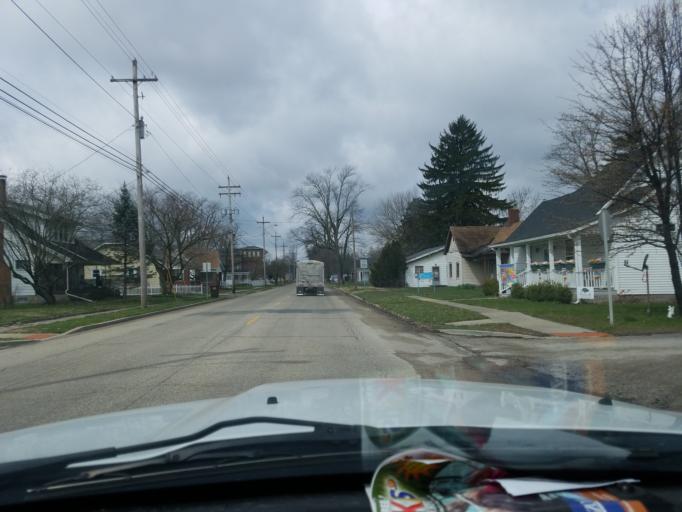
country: US
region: Indiana
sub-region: Vigo County
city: Seelyville
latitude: 39.3903
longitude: -87.2987
